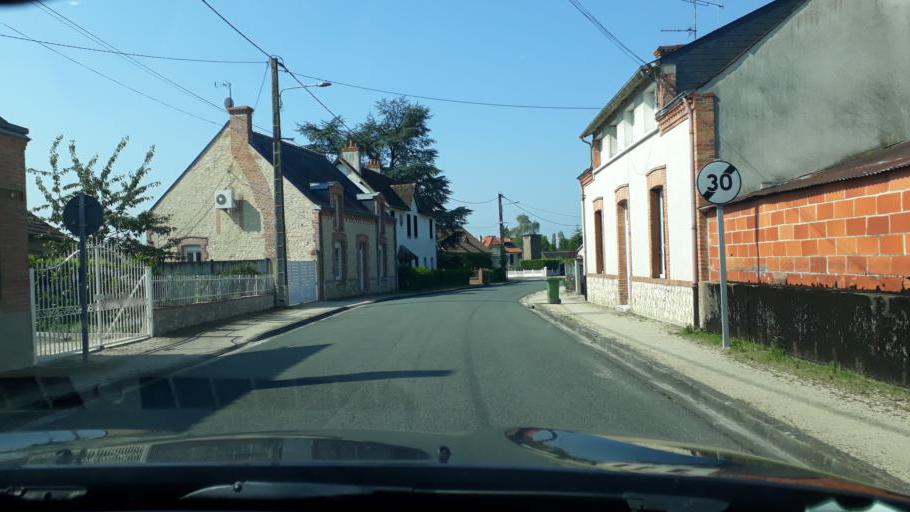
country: FR
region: Centre
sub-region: Departement du Loir-et-Cher
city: Dhuizon
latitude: 47.5884
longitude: 1.6574
